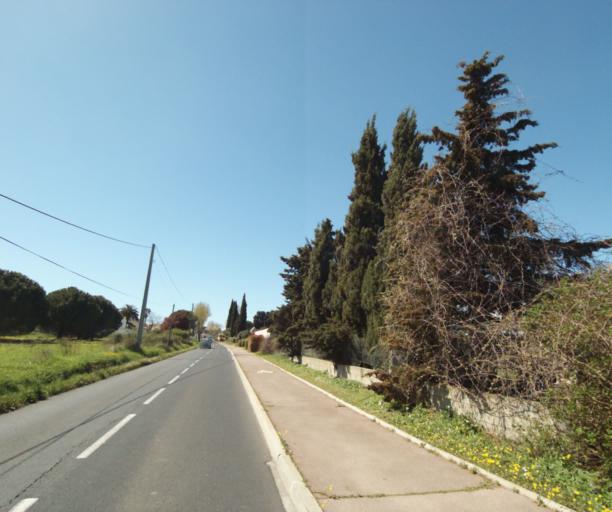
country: FR
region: Languedoc-Roussillon
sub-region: Departement de l'Herault
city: Villeneuve-les-Maguelone
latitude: 43.5365
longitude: 3.8677
